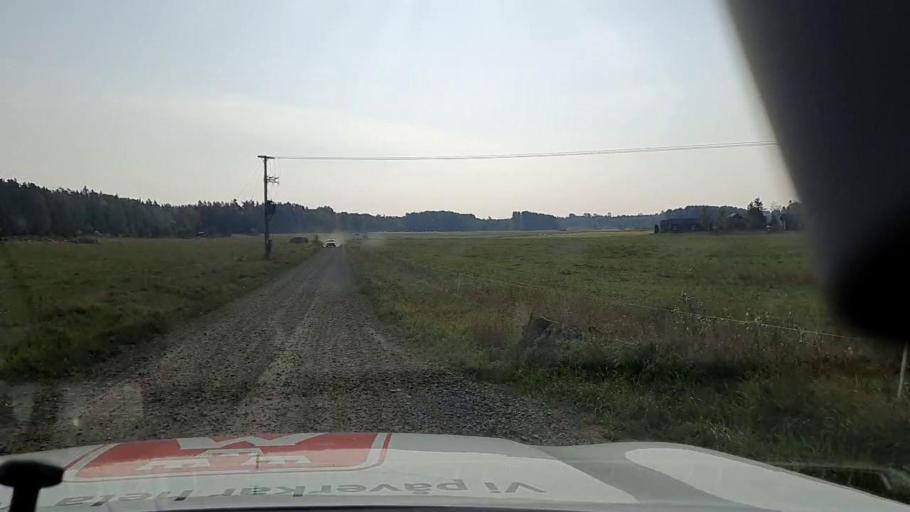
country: SE
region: Vaestmanland
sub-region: Kungsors Kommun
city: Kungsoer
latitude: 59.3552
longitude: 16.1583
